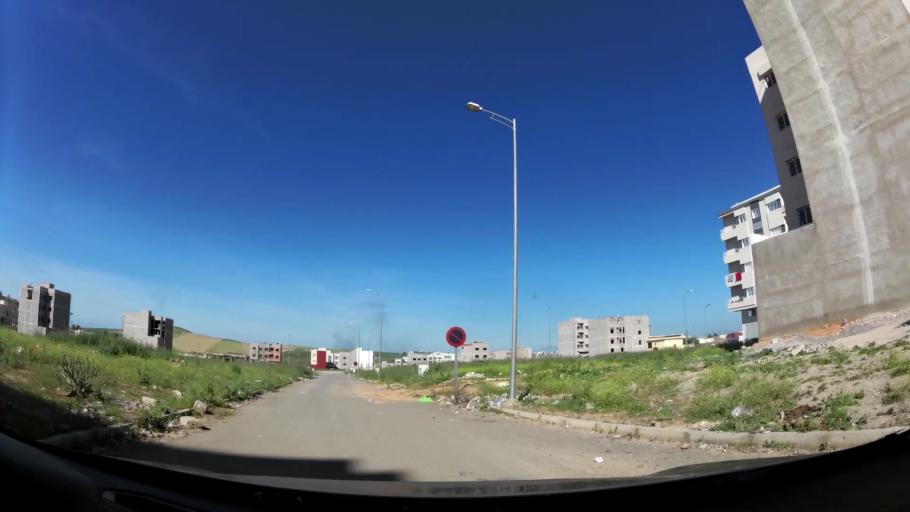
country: MA
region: Fes-Boulemane
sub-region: Fes
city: Fes
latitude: 34.0124
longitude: -4.9604
